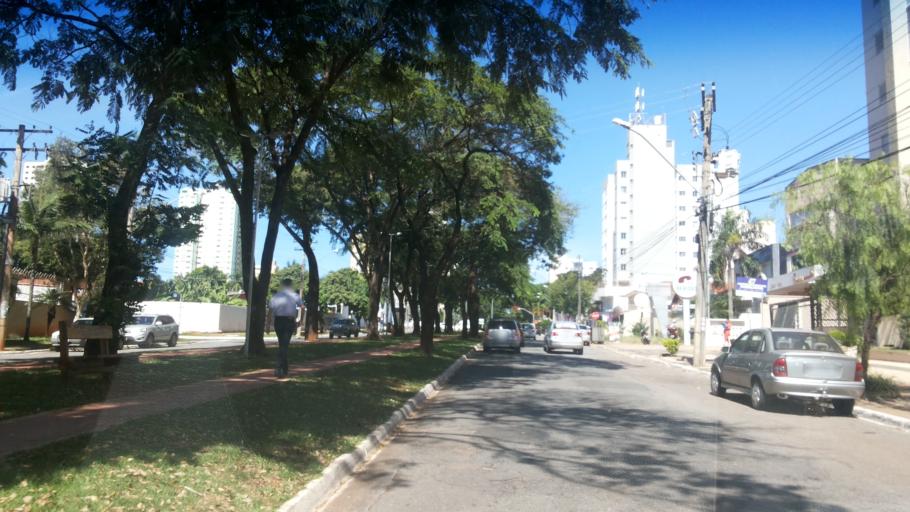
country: BR
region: Goias
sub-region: Goiania
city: Goiania
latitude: -16.7122
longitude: -49.2588
